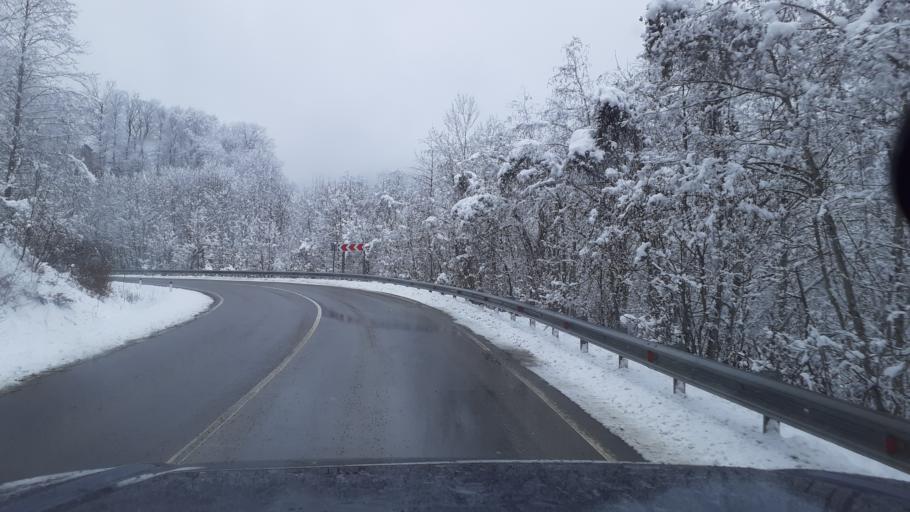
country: RU
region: Adygeya
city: Kamennomostskiy
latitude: 44.1821
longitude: 40.1575
